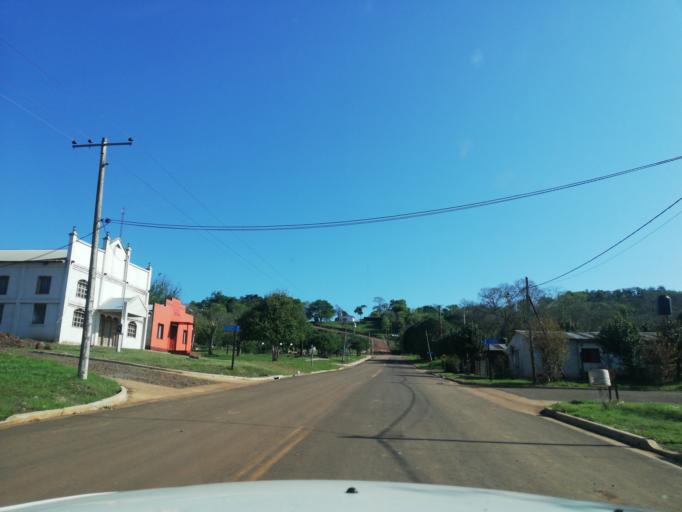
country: AR
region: Misiones
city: Arroyo del Medio
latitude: -27.6969
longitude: -55.4044
